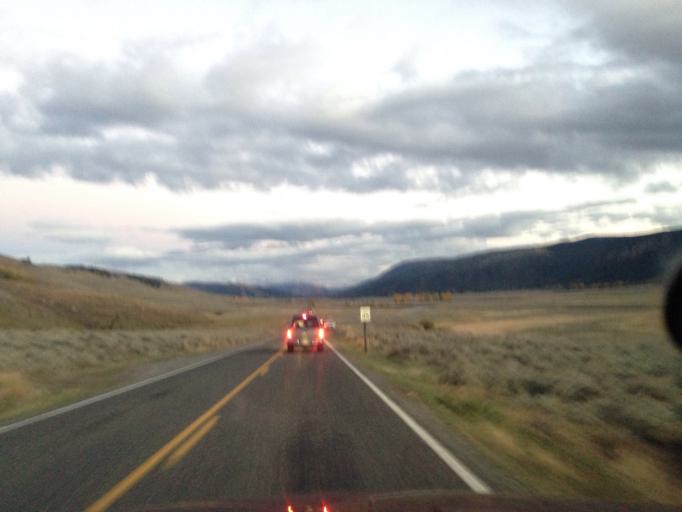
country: US
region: Montana
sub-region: Park County
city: Livingston
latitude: 44.8859
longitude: -110.2220
